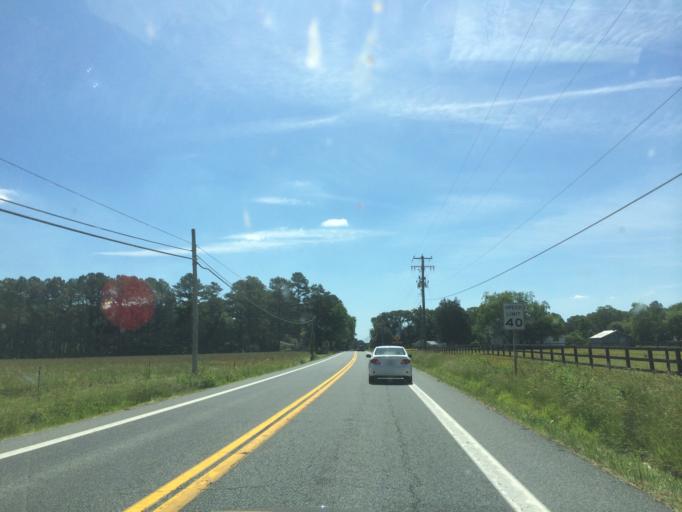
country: US
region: Maryland
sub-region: Wicomico County
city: Salisbury
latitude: 38.3231
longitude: -75.5563
